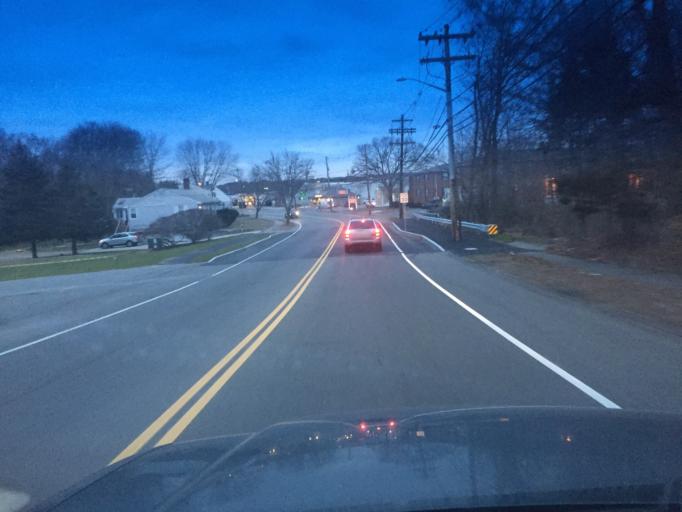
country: US
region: Massachusetts
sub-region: Norfolk County
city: Norwood
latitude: 42.1784
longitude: -71.1872
